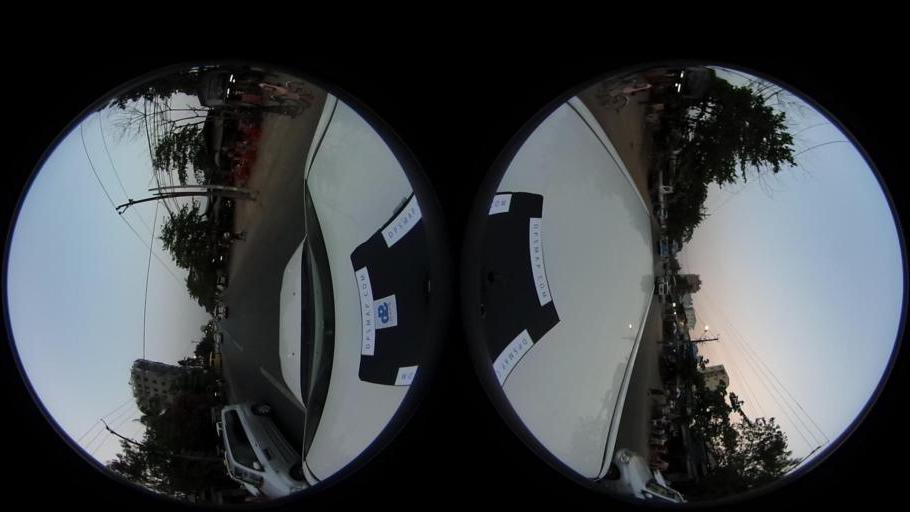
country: MM
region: Yangon
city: Yangon
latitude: 16.7878
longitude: 96.1910
